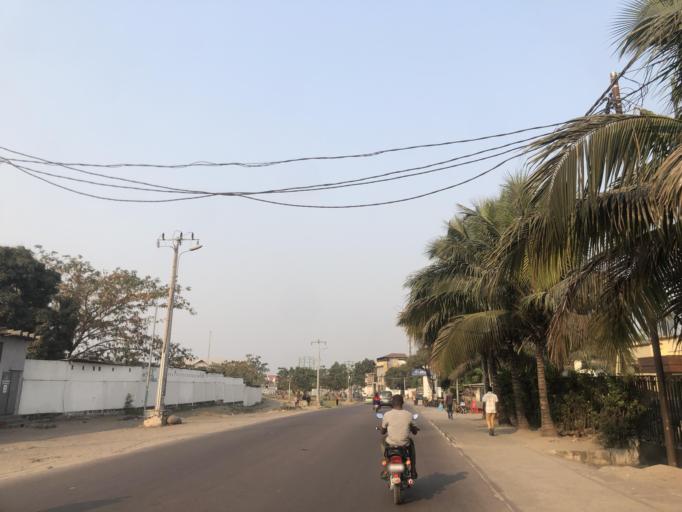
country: CD
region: Kinshasa
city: Kinshasa
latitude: -4.3302
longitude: 15.3269
